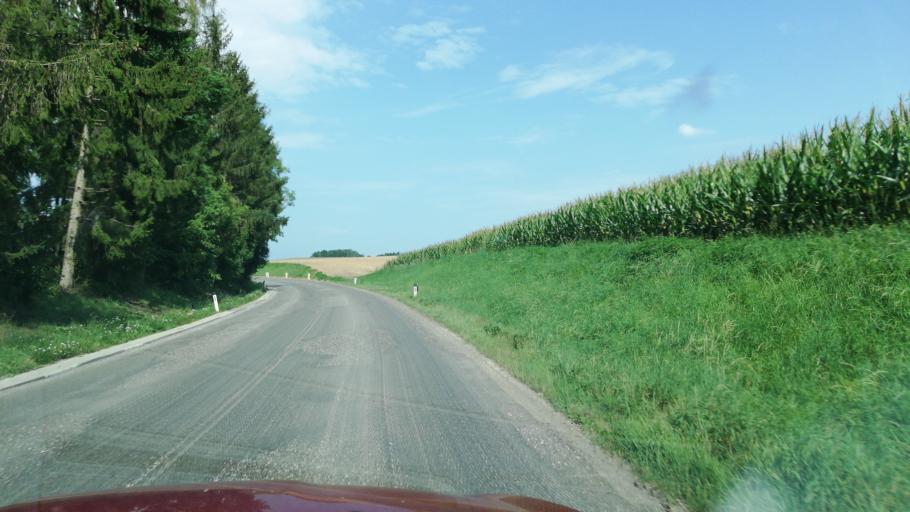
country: AT
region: Upper Austria
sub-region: Politischer Bezirk Steyr-Land
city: Sierning
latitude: 48.1085
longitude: 14.3230
